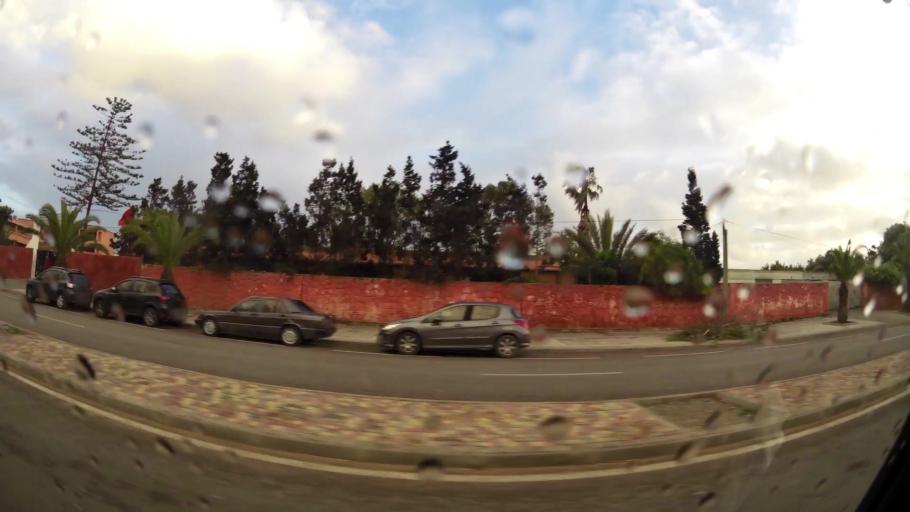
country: MA
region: Doukkala-Abda
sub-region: El-Jadida
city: El Jadida
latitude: 33.2415
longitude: -8.5020
